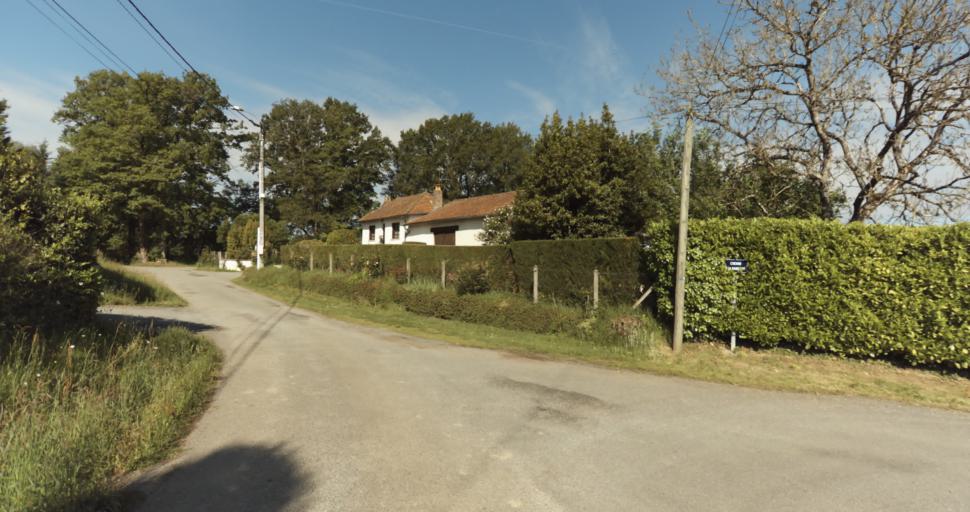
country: FR
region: Limousin
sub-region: Departement de la Haute-Vienne
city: Solignac
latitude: 45.7197
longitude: 1.2464
